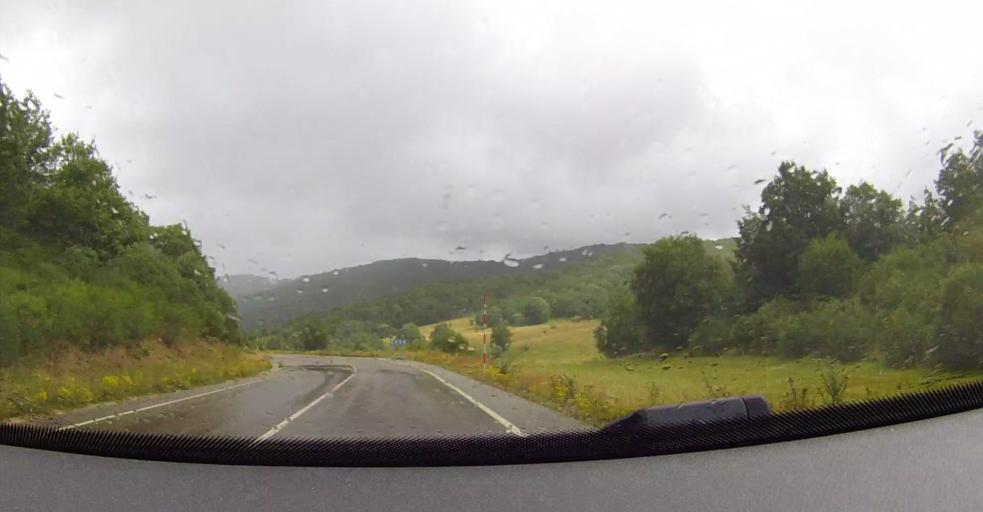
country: ES
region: Castille and Leon
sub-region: Provincia de Leon
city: Marana
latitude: 43.0710
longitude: -5.1927
